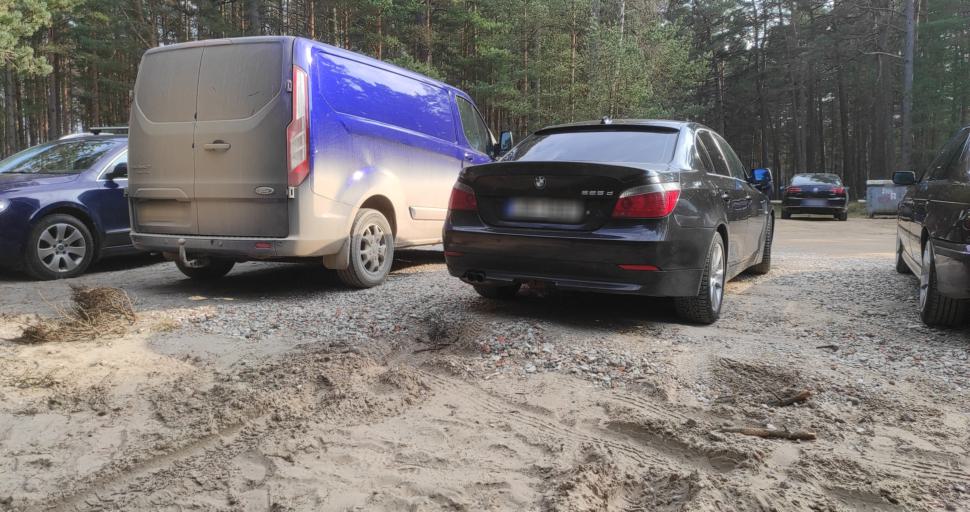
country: LV
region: Nica
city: Nica
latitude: 56.3292
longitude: 20.9924
